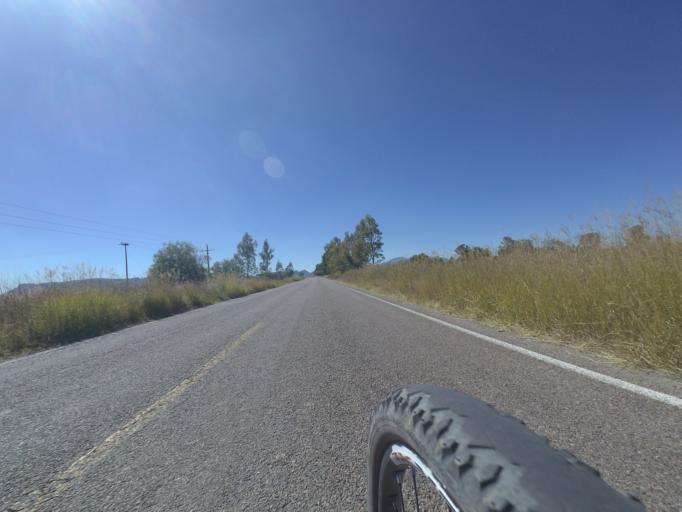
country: MX
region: Aguascalientes
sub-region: Aguascalientes
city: Los Canos
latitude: 21.8710
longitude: -102.4987
